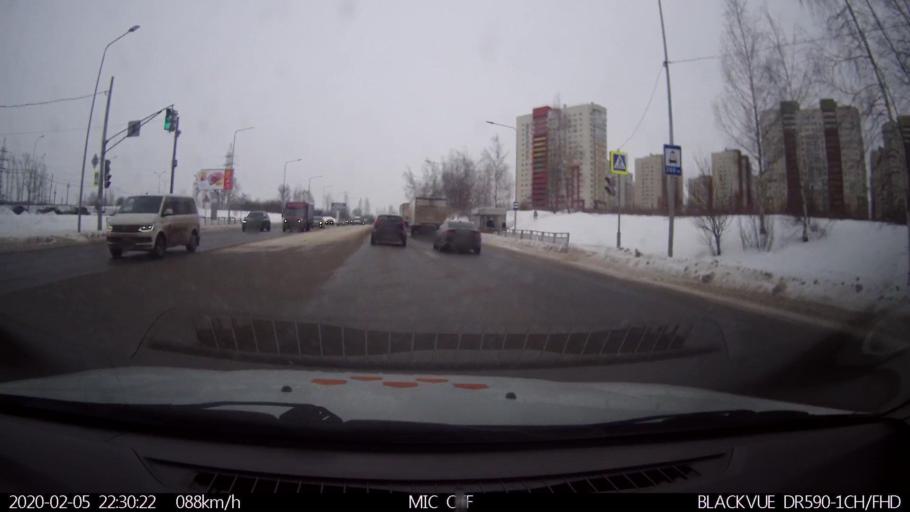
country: RU
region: Nizjnij Novgorod
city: Imeni Stepana Razina
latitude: 54.7434
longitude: 44.1598
